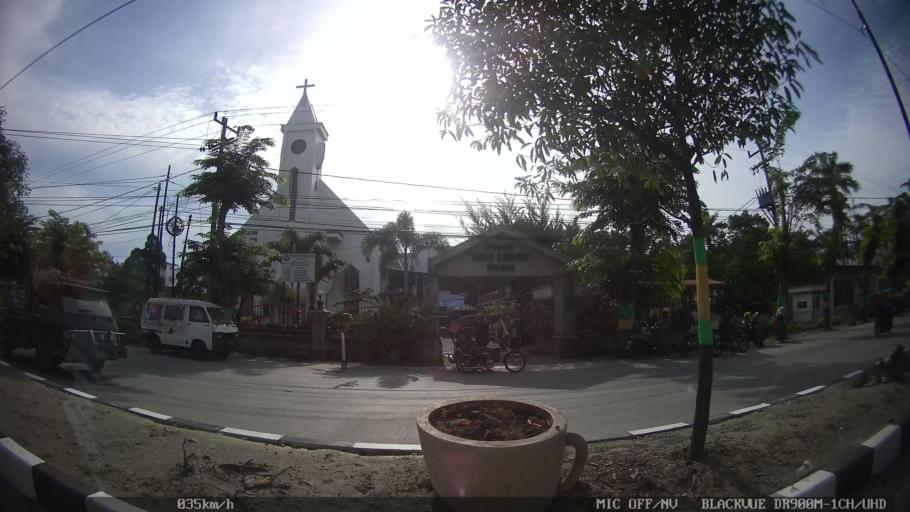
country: ID
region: North Sumatra
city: Medan
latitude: 3.5992
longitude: 98.6450
